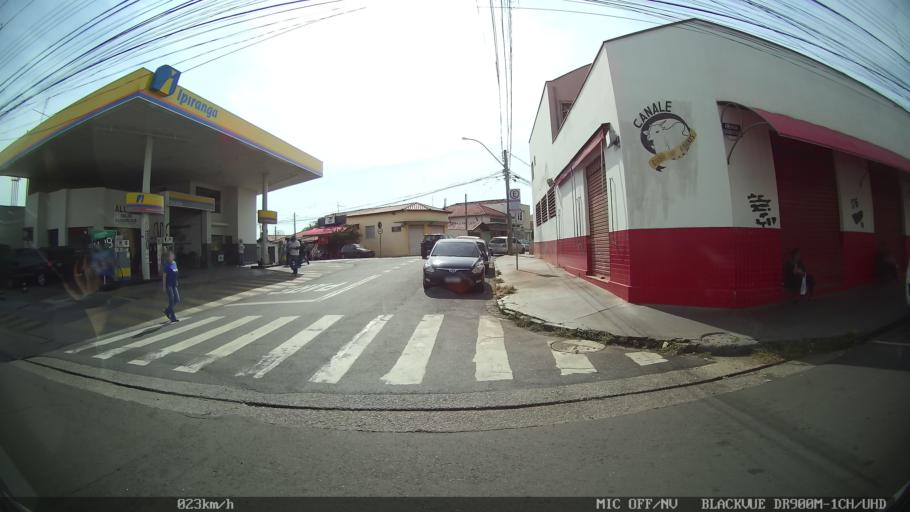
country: BR
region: Sao Paulo
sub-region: Piracicaba
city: Piracicaba
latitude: -22.7383
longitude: -47.6596
